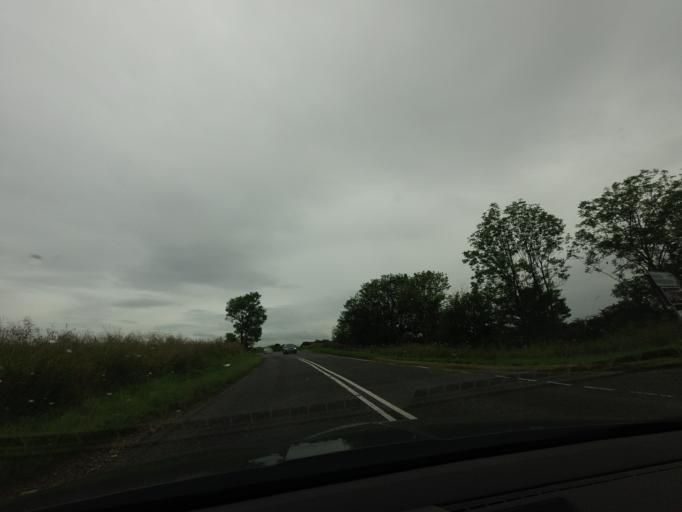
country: GB
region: Scotland
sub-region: Aberdeenshire
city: Portsoy
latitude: 57.6742
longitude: -2.6872
